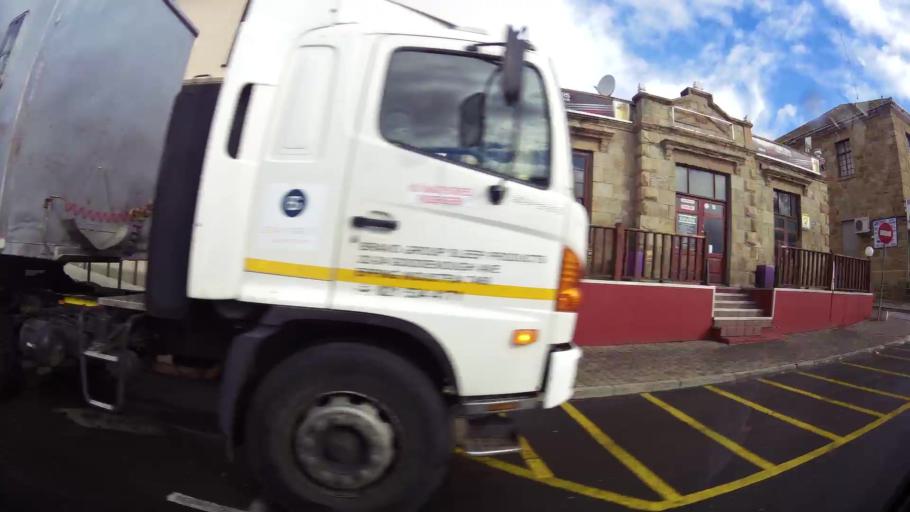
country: ZA
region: Western Cape
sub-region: Eden District Municipality
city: Mossel Bay
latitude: -34.1814
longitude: 22.1442
